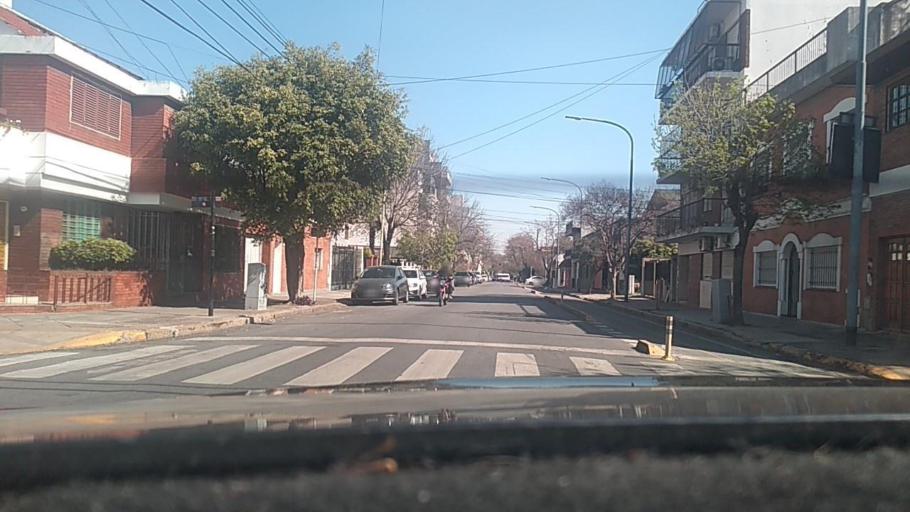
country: AR
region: Buenos Aires F.D.
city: Villa Santa Rita
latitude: -34.6120
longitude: -58.5024
